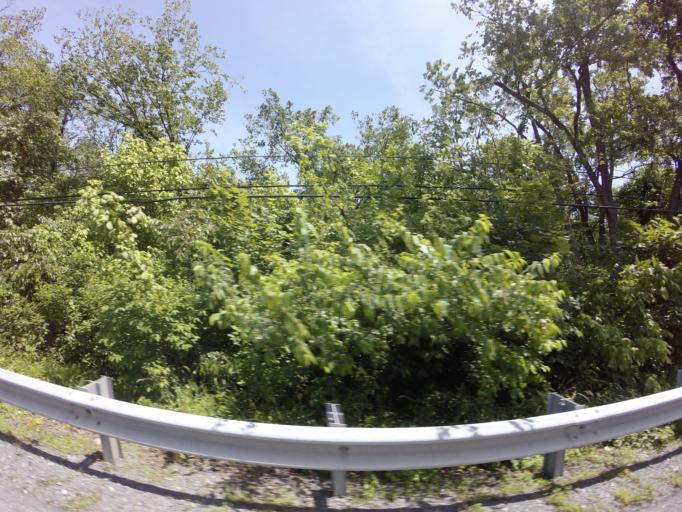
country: US
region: Maryland
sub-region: Frederick County
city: Urbana
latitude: 39.3472
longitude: -77.3761
